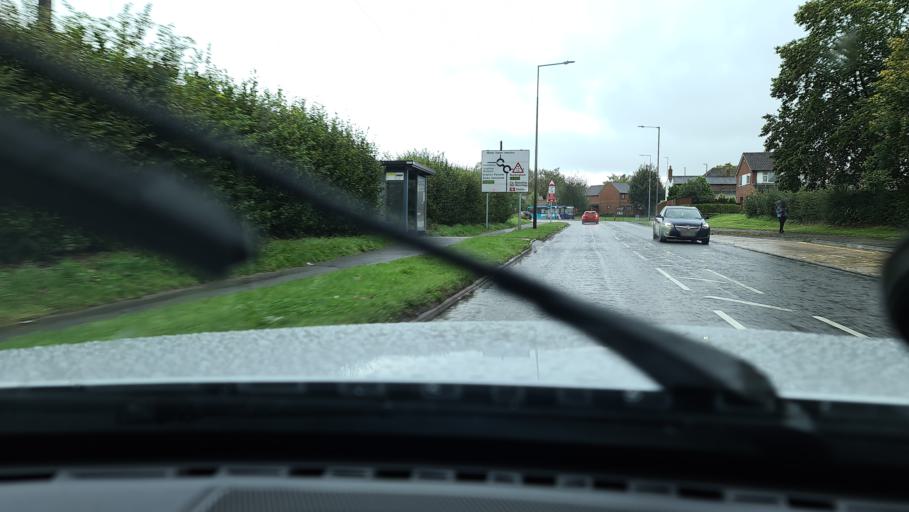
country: GB
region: England
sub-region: Milton Keynes
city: Water Eaton
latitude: 51.9904
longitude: -0.7218
